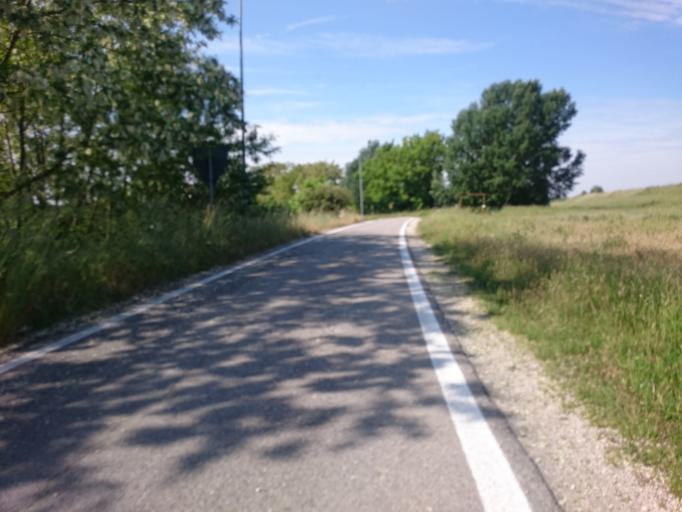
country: IT
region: Veneto
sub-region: Provincia di Rovigo
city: Bottrighe
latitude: 45.0143
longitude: 12.0837
